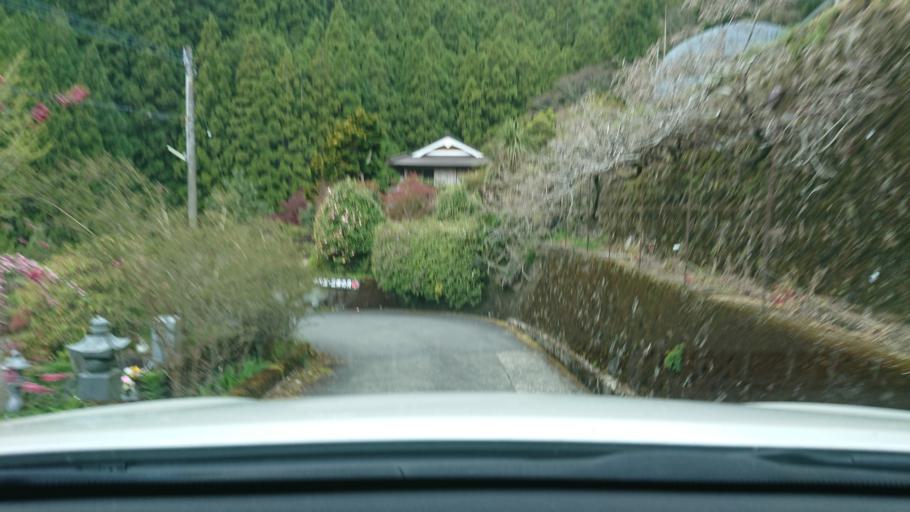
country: JP
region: Tokushima
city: Kamojimacho-jogejima
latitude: 33.8860
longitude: 134.3768
